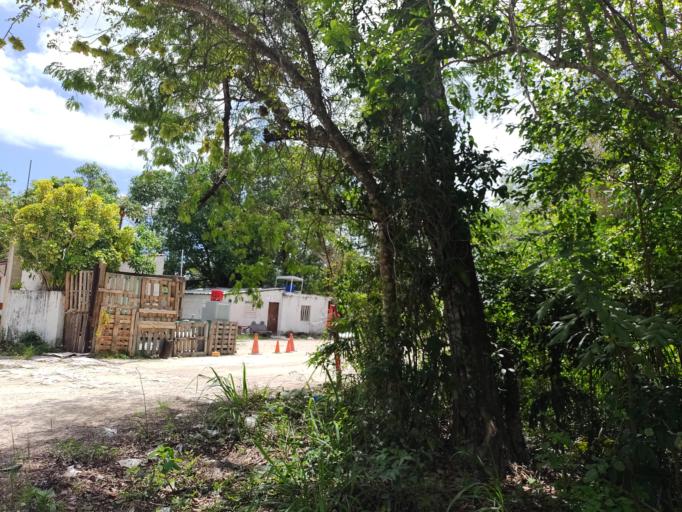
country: MX
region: Quintana Roo
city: San Miguel de Cozumel
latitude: 20.4872
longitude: -86.9097
